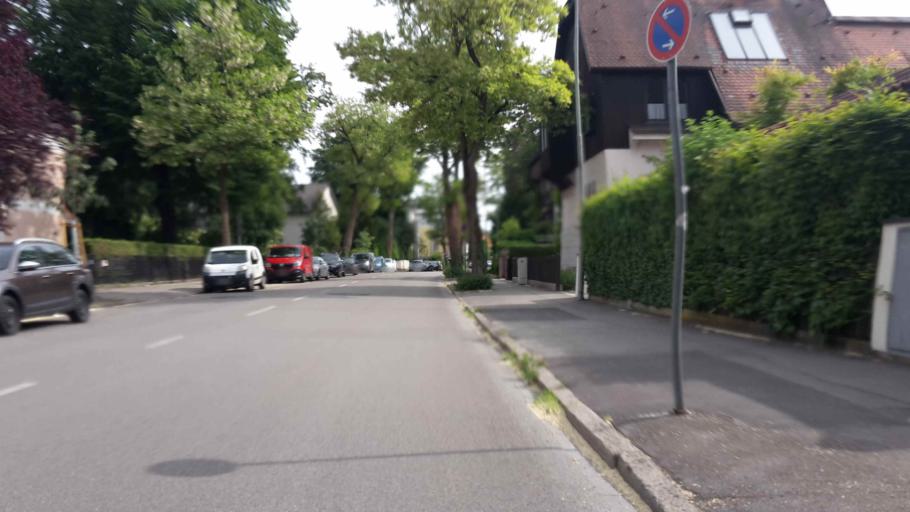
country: DE
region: Bavaria
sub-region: Upper Bavaria
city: Dachau
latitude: 48.2514
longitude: 11.4409
